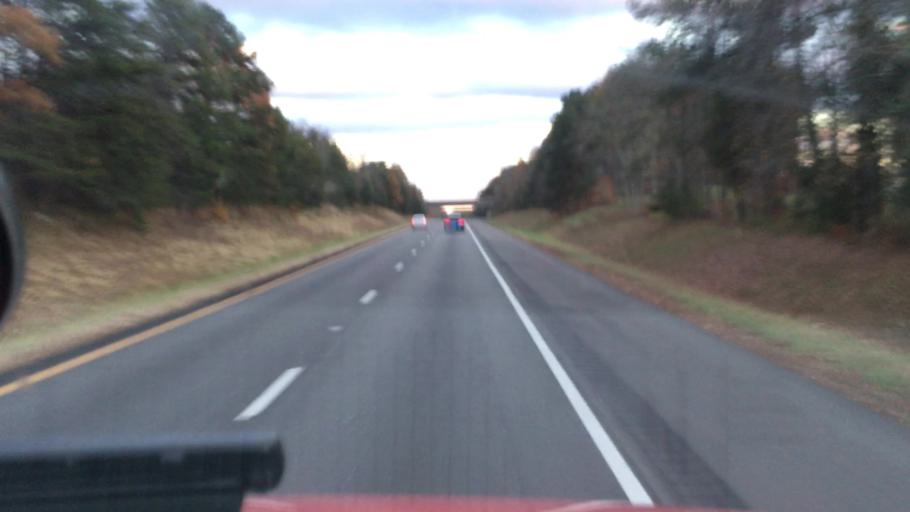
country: US
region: Virginia
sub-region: Fluvanna County
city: Palmyra
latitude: 37.9783
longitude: -78.2172
